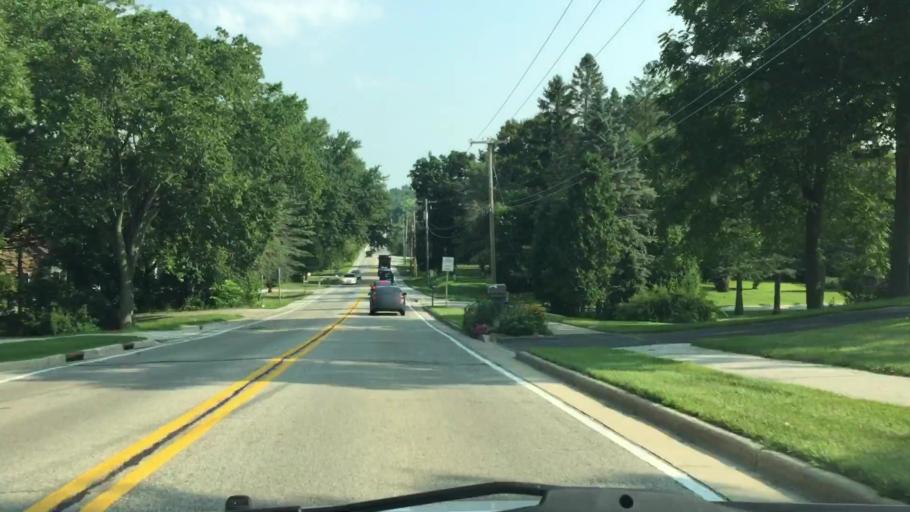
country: US
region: Wisconsin
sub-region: Waukesha County
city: Brookfield
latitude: 43.0412
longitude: -88.1466
